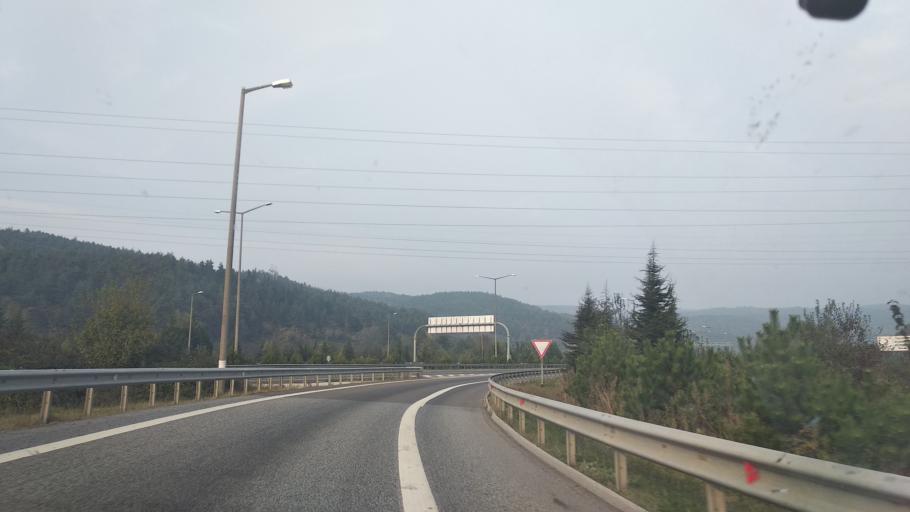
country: TR
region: Duzce
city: Kaynasli
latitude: 40.7872
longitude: 31.2771
